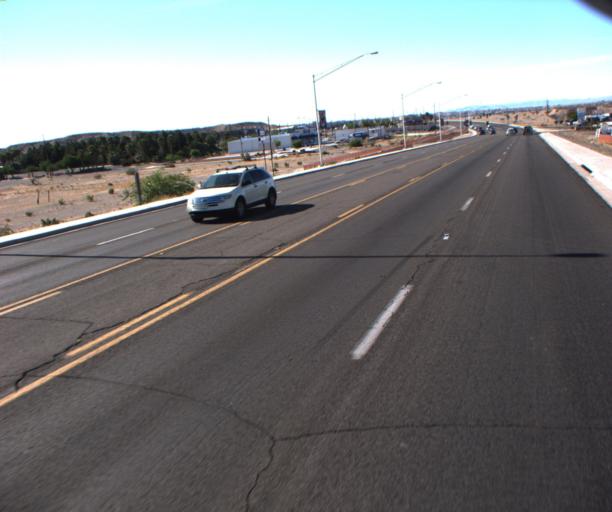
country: US
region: Arizona
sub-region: Mohave County
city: Bullhead City
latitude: 35.0875
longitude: -114.5980
